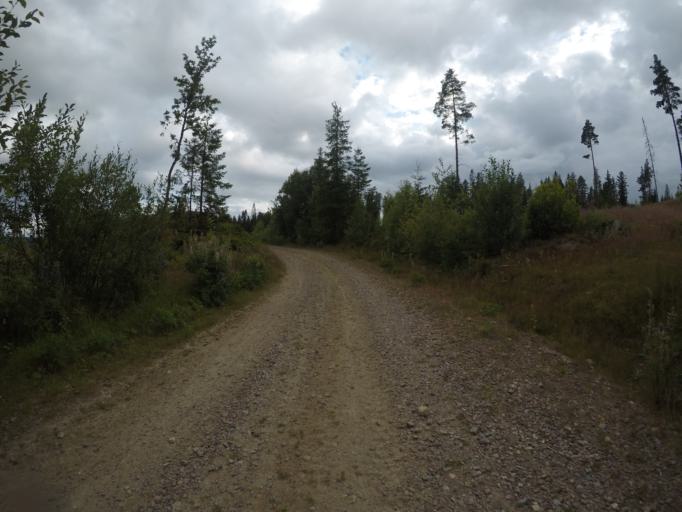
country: SE
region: Vaermland
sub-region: Filipstads Kommun
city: Lesjofors
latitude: 60.1502
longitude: 14.3929
